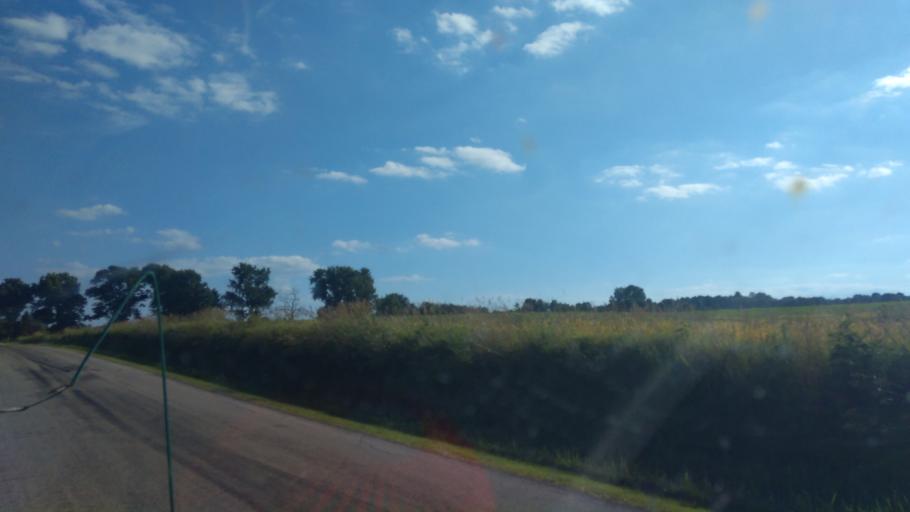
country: US
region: Ohio
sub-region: Wayne County
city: Shreve
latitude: 40.7339
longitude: -82.1075
